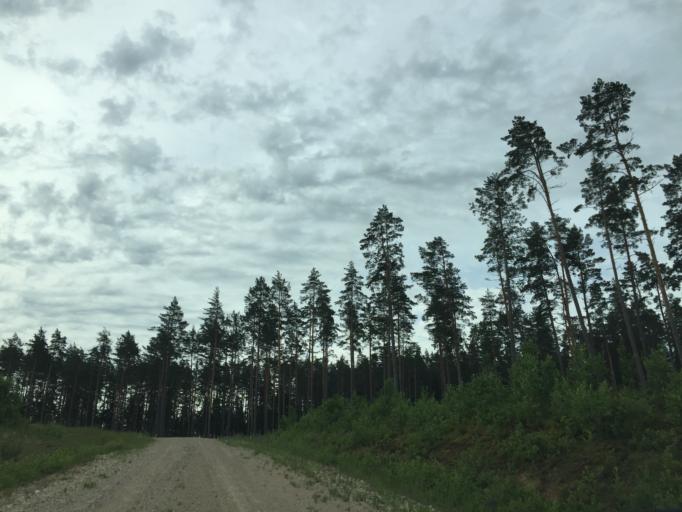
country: LV
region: Tukuma Rajons
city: Tukums
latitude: 57.0303
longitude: 23.1608
